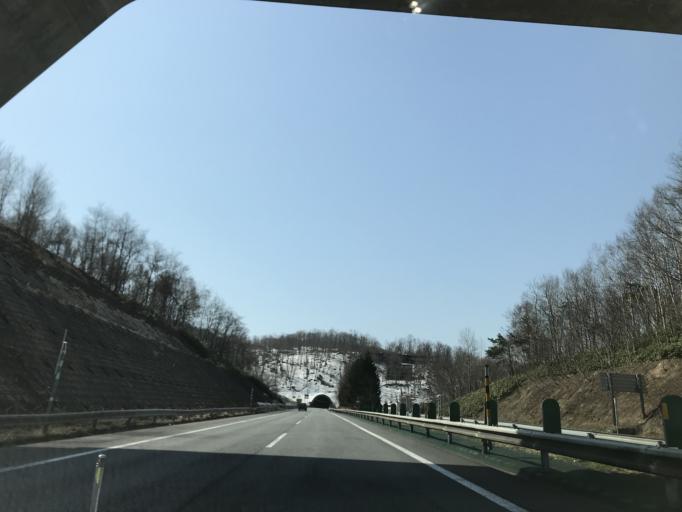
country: JP
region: Hokkaido
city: Bibai
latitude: 43.3108
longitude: 141.8819
